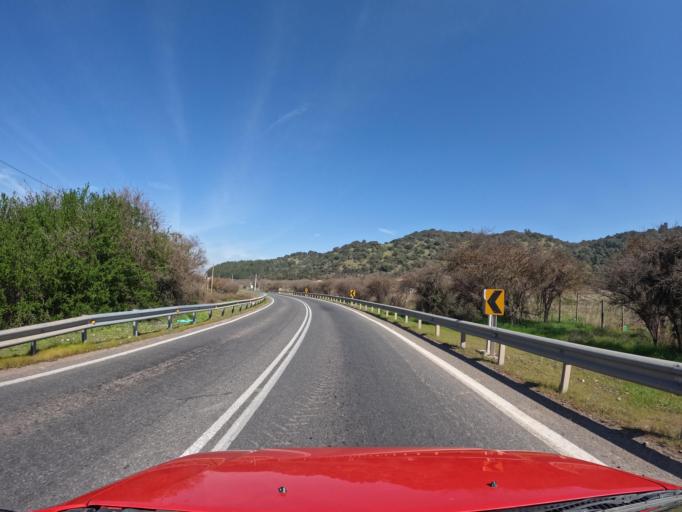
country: CL
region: Maule
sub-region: Provincia de Curico
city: Rauco
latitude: -34.9809
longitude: -71.4205
